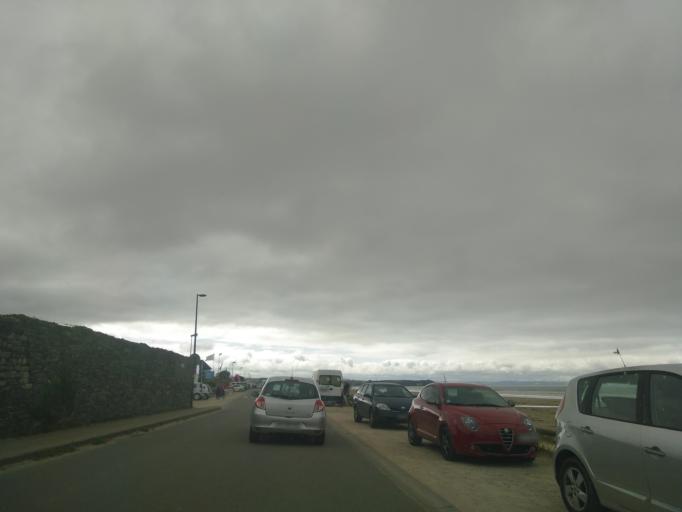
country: FR
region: Brittany
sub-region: Departement du Finistere
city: Telgruc-sur-Mer
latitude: 48.1933
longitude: -4.3020
